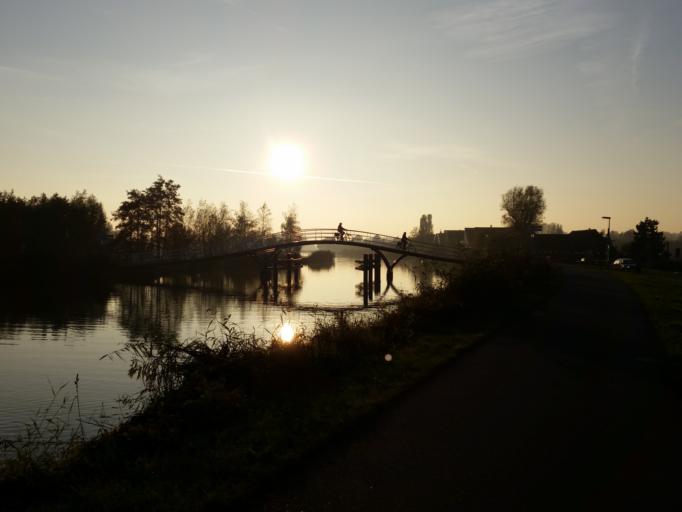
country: NL
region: South Holland
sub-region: Gemeente Lansingerland
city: Bleiswijk
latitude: 51.9731
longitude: 4.5479
